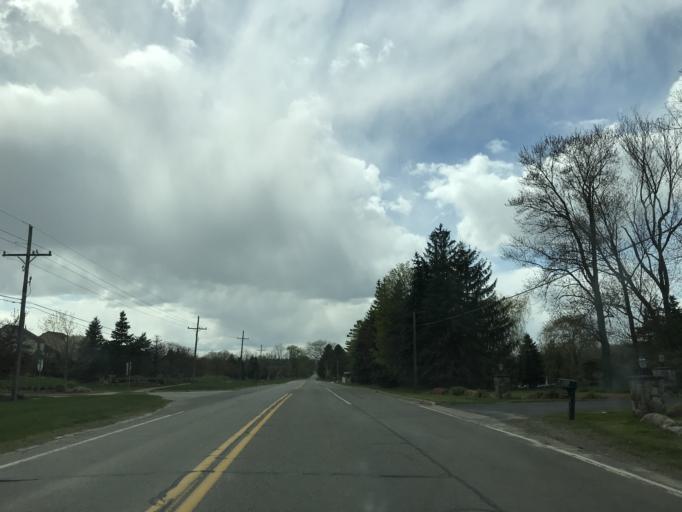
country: US
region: Michigan
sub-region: Wayne County
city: Plymouth
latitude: 42.3748
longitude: -83.5444
